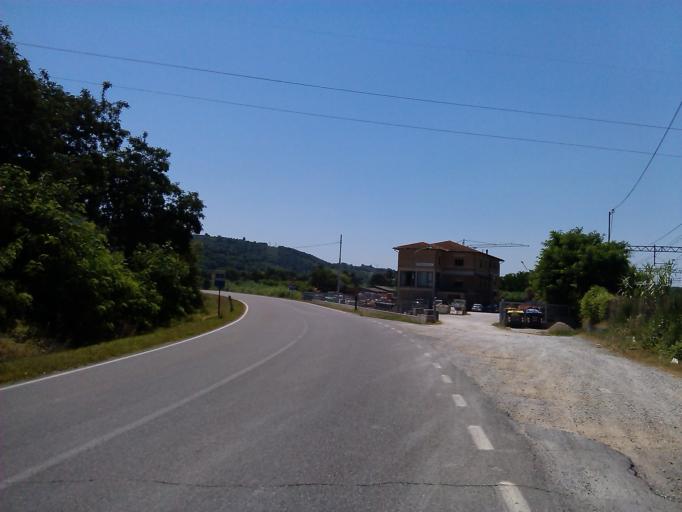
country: IT
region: Umbria
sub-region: Provincia di Terni
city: Fabro Scalo
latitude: 42.8710
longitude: 12.0421
